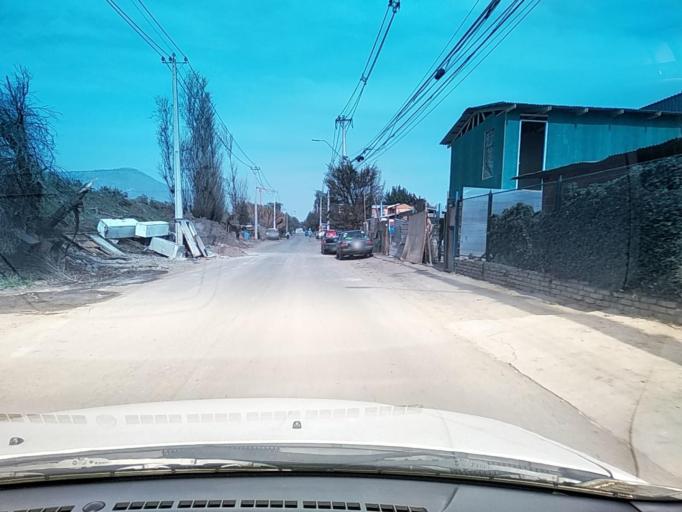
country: CL
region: Santiago Metropolitan
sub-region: Provincia de Chacabuco
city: Chicureo Abajo
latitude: -33.2998
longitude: -70.7211
